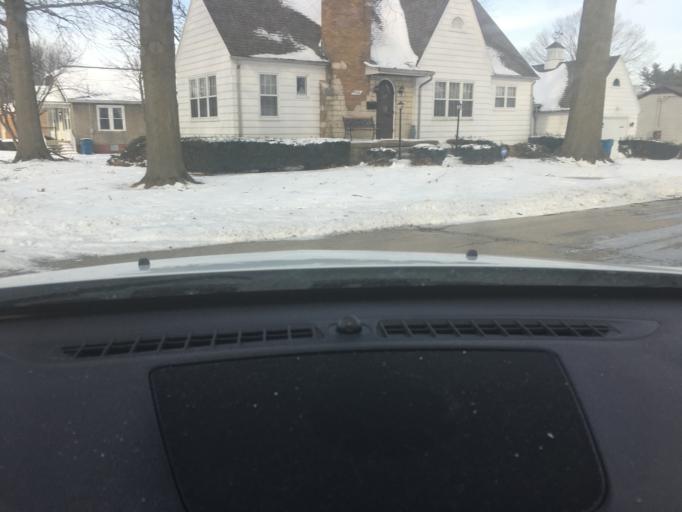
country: US
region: Illinois
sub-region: LaSalle County
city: Peru
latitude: 41.3351
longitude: -89.1144
